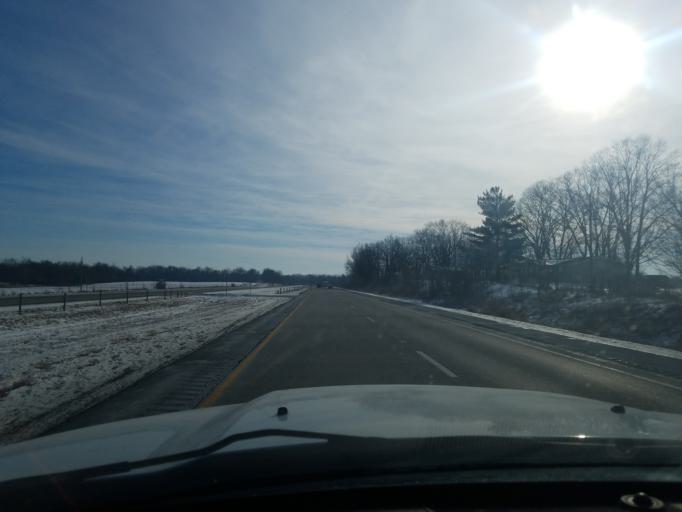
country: US
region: Indiana
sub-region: Grant County
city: Upland
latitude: 40.4669
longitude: -85.5506
